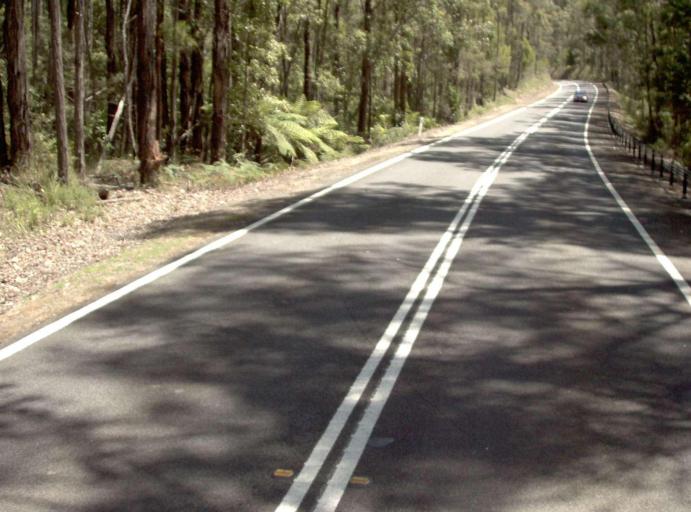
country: AU
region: New South Wales
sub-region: Bombala
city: Bombala
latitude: -37.5826
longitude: 148.9222
